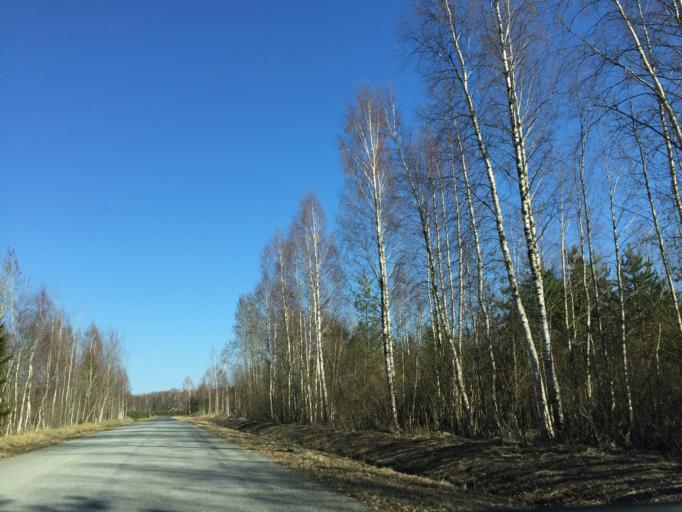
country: EE
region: Ida-Virumaa
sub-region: Johvi vald
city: Johvi
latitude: 59.0130
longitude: 27.5362
